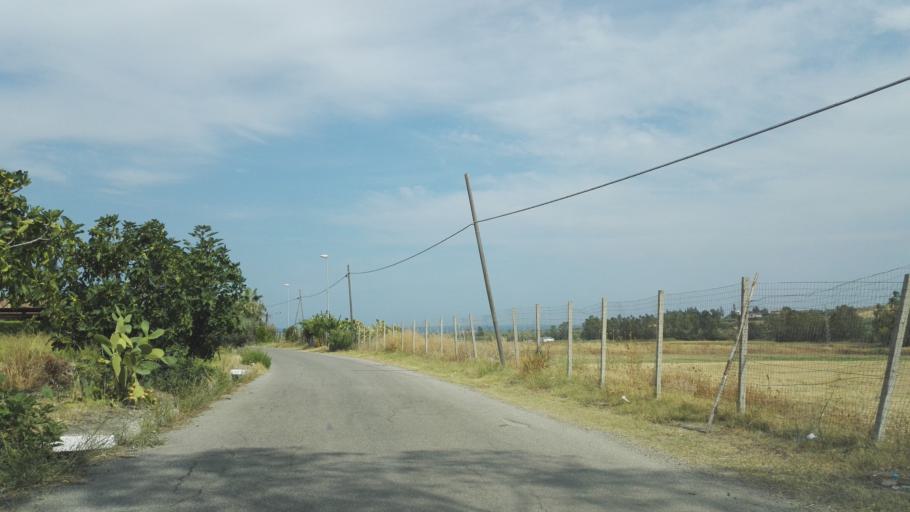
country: IT
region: Calabria
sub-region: Provincia di Reggio Calabria
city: Monasterace Marina
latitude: 38.4261
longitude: 16.5489
